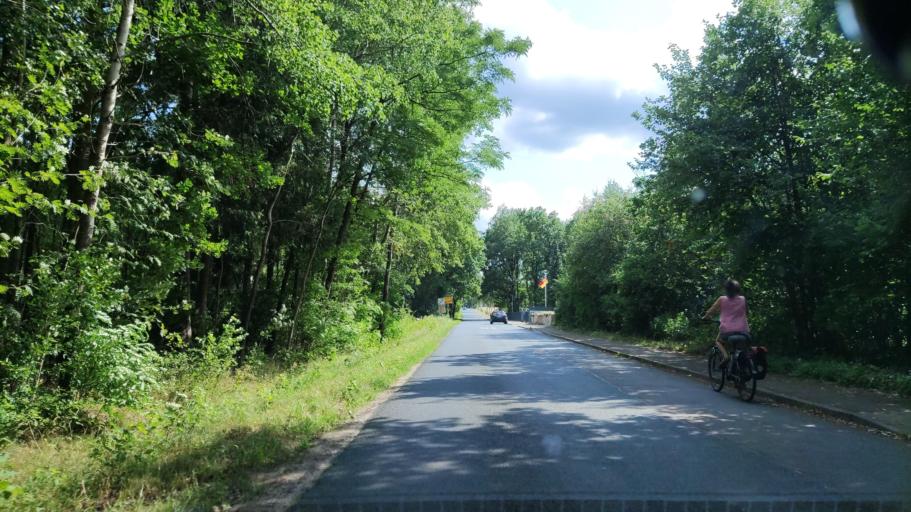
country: DE
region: Lower Saxony
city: Soltau
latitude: 53.0135
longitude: 9.8725
